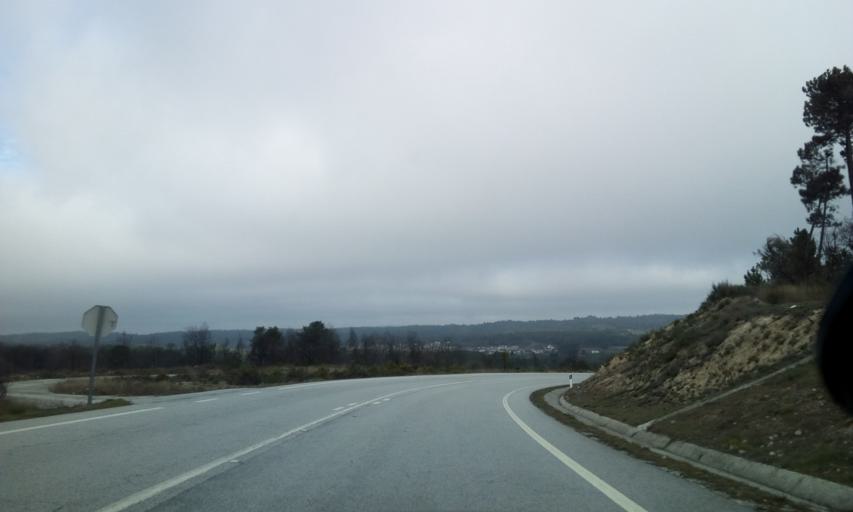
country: PT
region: Guarda
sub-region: Fornos de Algodres
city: Fornos de Algodres
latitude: 40.7079
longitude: -7.4845
